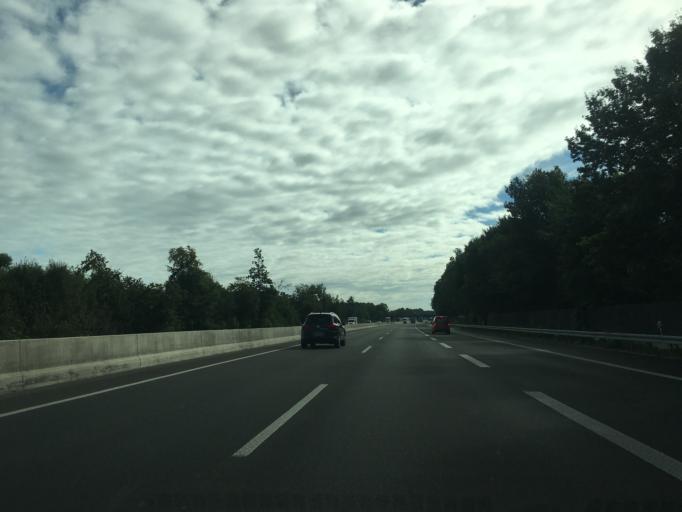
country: DE
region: North Rhine-Westphalia
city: Buende
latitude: 52.1943
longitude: 8.5396
